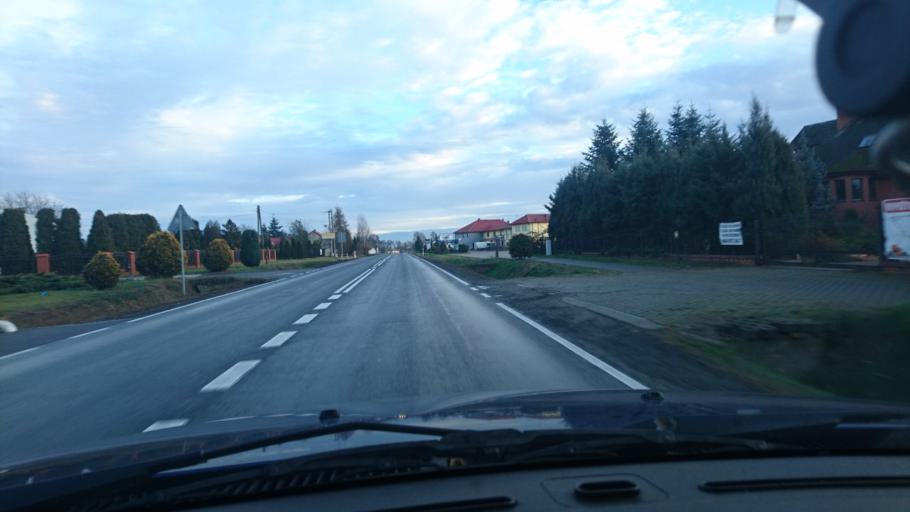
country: PL
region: Greater Poland Voivodeship
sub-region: Powiat kepinski
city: Leka Opatowska
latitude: 51.2286
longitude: 18.0798
